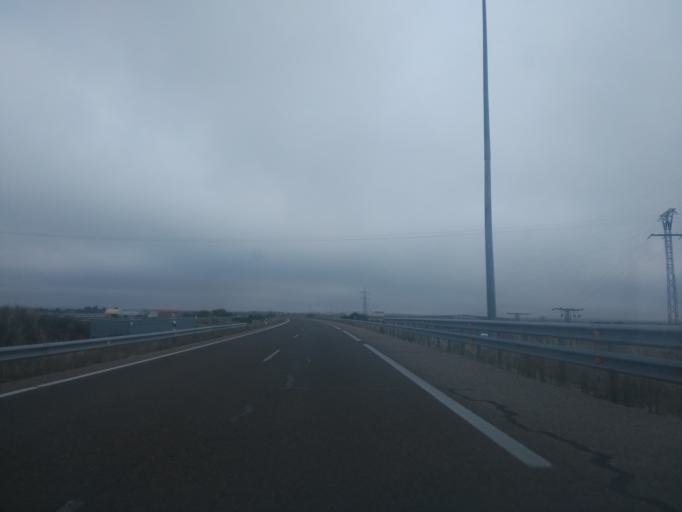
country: ES
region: Castille and Leon
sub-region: Provincia de Salamanca
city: Castellanos de Moriscos
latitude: 41.0134
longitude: -5.5869
